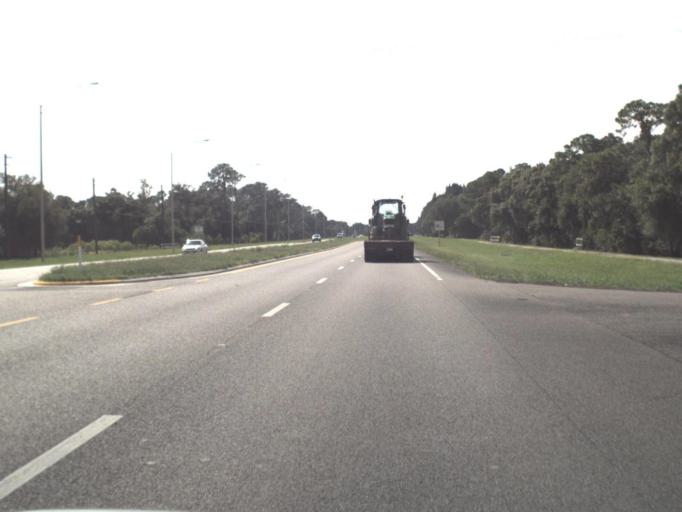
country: US
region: Florida
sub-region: Manatee County
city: Ellenton
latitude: 27.4843
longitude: -82.4126
